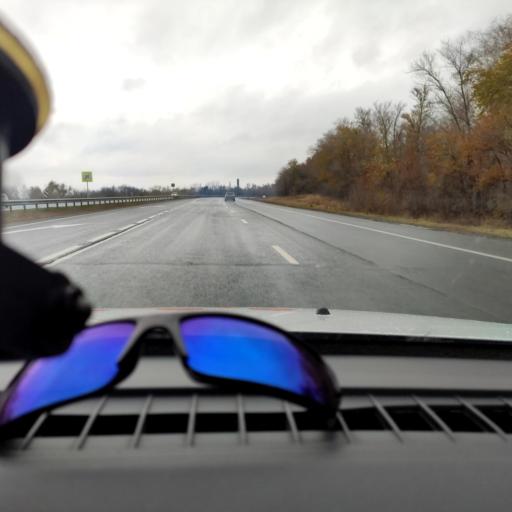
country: RU
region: Samara
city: Novokuybyshevsk
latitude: 53.0480
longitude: 50.0079
